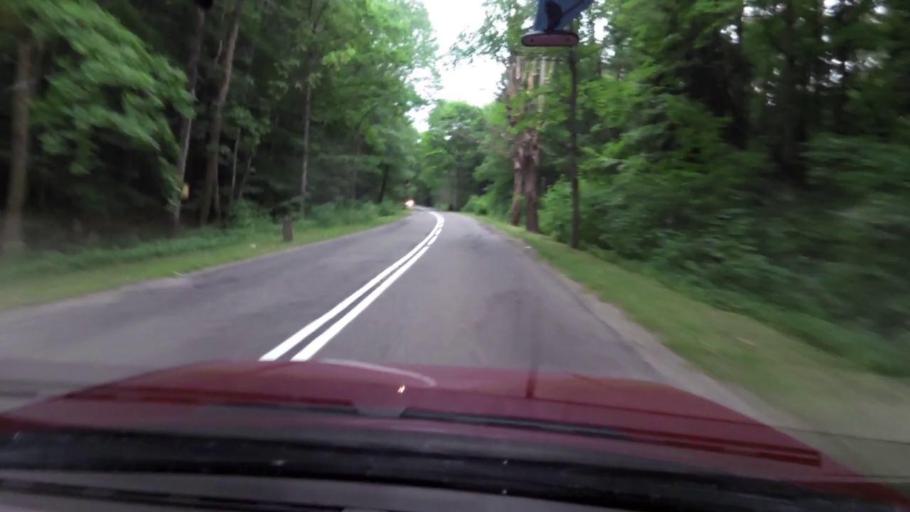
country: PL
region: West Pomeranian Voivodeship
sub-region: Powiat koszalinski
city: Sianow
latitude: 54.1894
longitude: 16.2920
